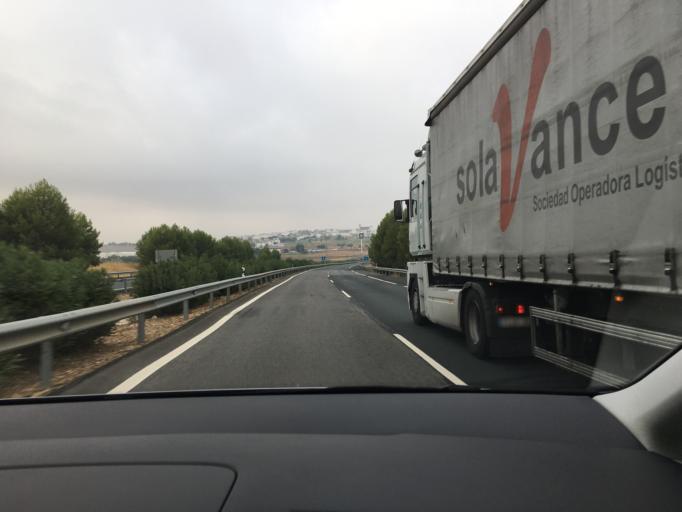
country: ES
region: Andalusia
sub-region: Province of Cordoba
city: La Carlota
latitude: 37.6851
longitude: -4.9246
